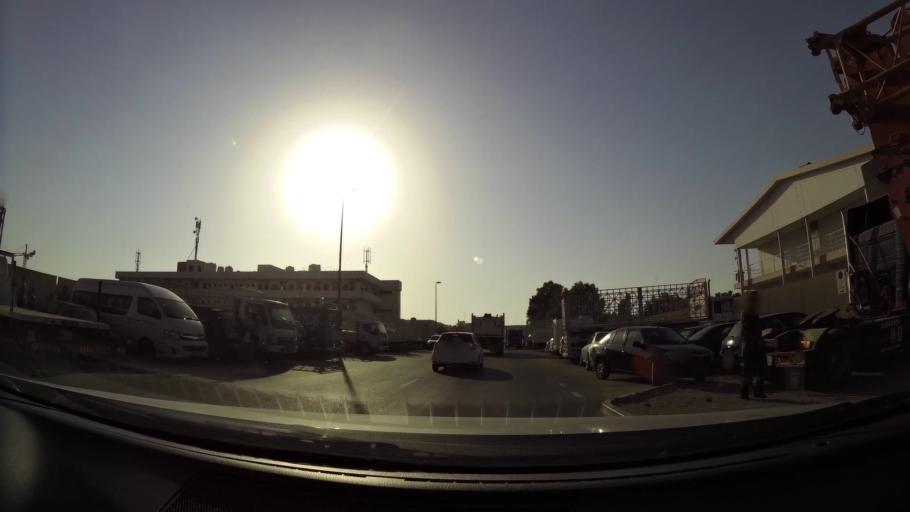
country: AE
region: Dubai
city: Dubai
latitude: 25.1284
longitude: 55.2367
